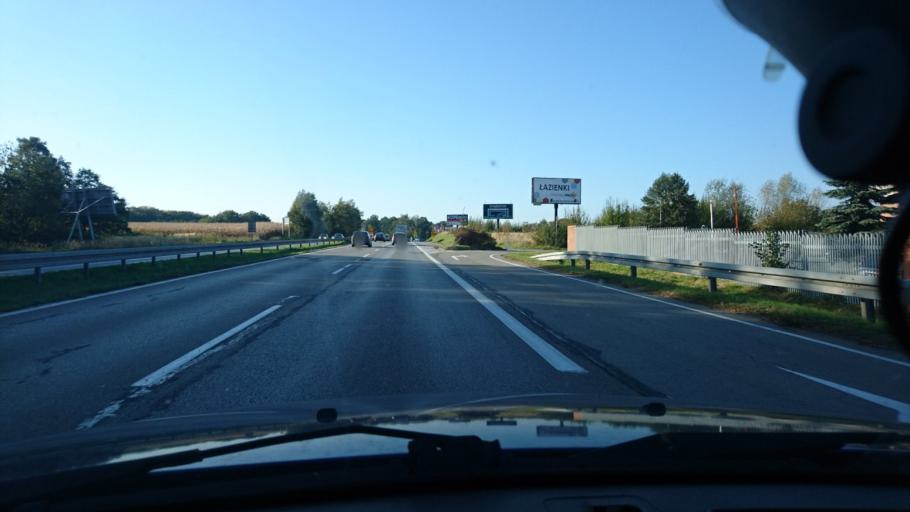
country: PL
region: Silesian Voivodeship
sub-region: Powiat bielski
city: Mazancowice
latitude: 49.8616
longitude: 19.0186
